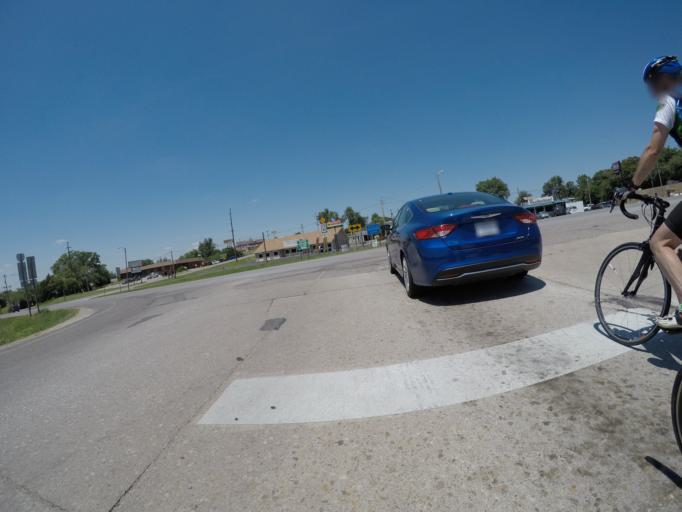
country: US
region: Kansas
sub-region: Geary County
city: Grandview Plaza
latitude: 39.0281
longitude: -96.8003
